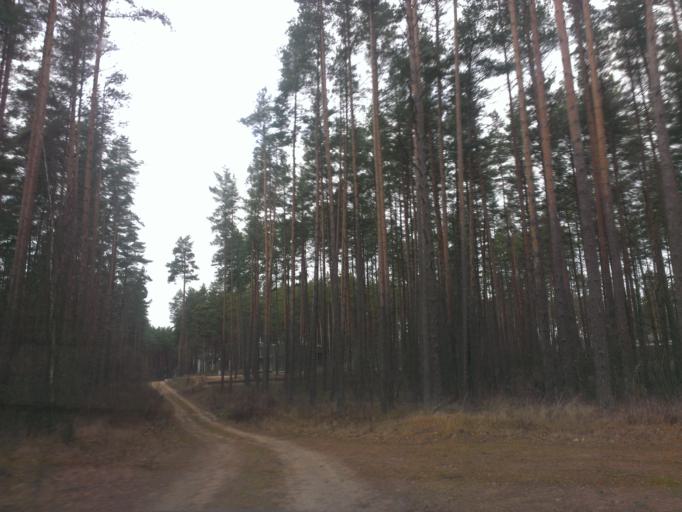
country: LV
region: Riga
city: Bergi
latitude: 56.9916
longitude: 24.3070
